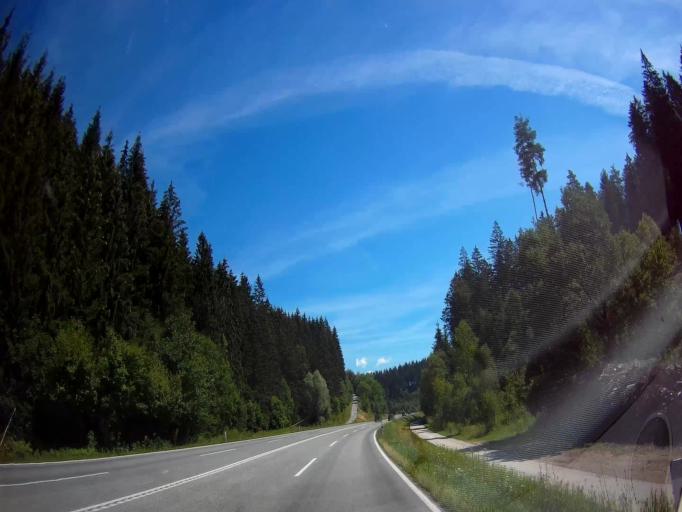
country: AT
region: Carinthia
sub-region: Politischer Bezirk Sankt Veit an der Glan
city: St. Georgen am Laengsee
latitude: 46.8133
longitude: 14.4267
